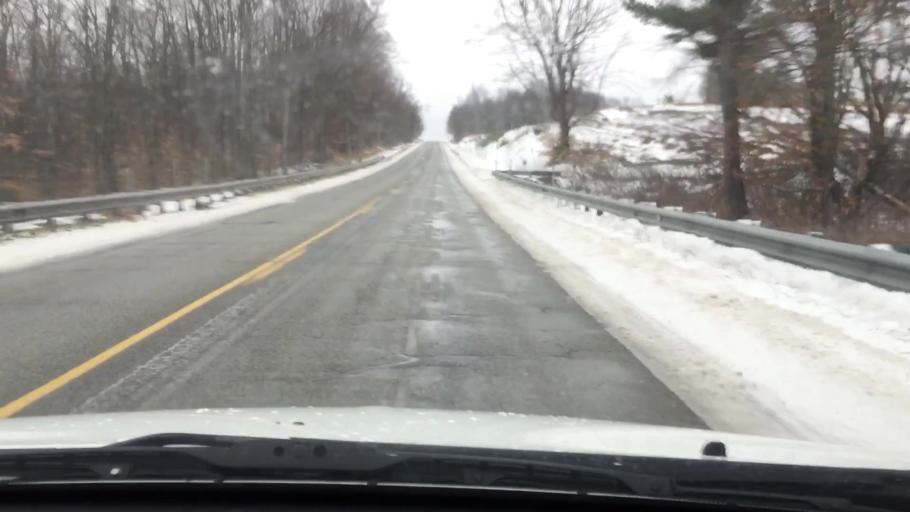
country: US
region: Michigan
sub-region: Wexford County
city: Cadillac
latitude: 44.1716
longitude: -85.4054
